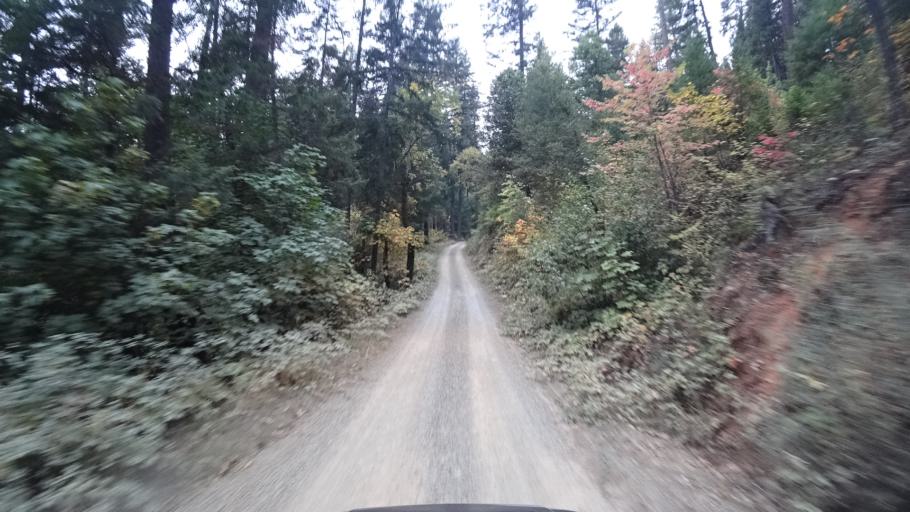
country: US
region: California
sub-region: Siskiyou County
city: Happy Camp
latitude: 41.7908
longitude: -123.3379
